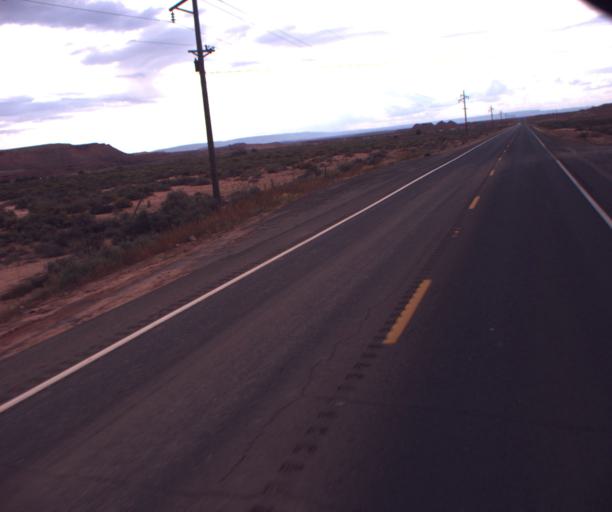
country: US
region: Arizona
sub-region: Coconino County
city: Tuba City
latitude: 36.1056
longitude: -111.2647
